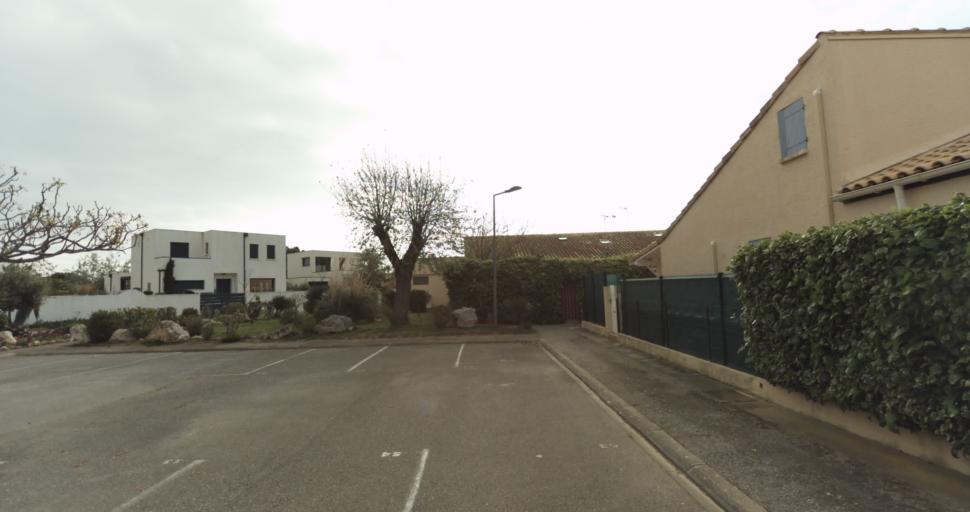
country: FR
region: Languedoc-Roussillon
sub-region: Departement de l'Aude
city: Leucate
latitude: 42.9354
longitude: 3.0258
